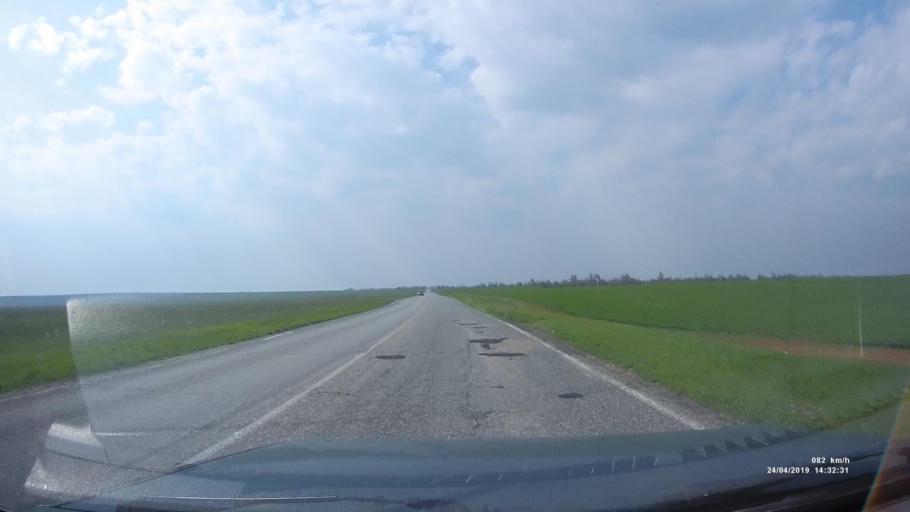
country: RU
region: Kalmykiya
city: Arshan'
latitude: 46.3653
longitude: 43.9676
